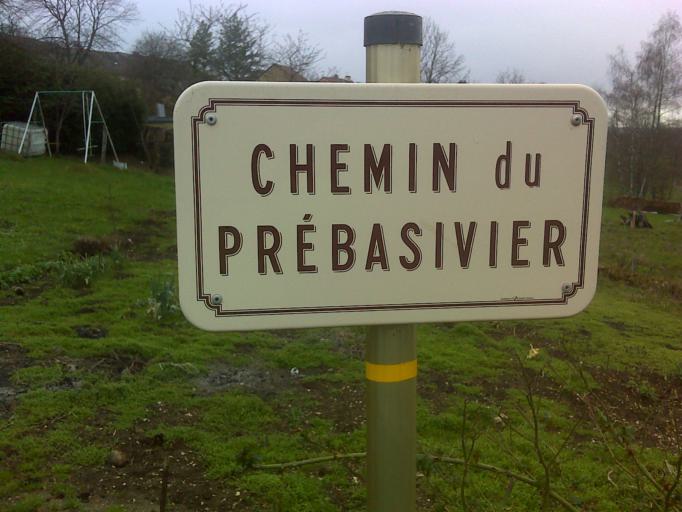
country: FR
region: Franche-Comte
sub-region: Departement du Jura
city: Clairvaux-les-Lacs
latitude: 46.6014
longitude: 5.8547
